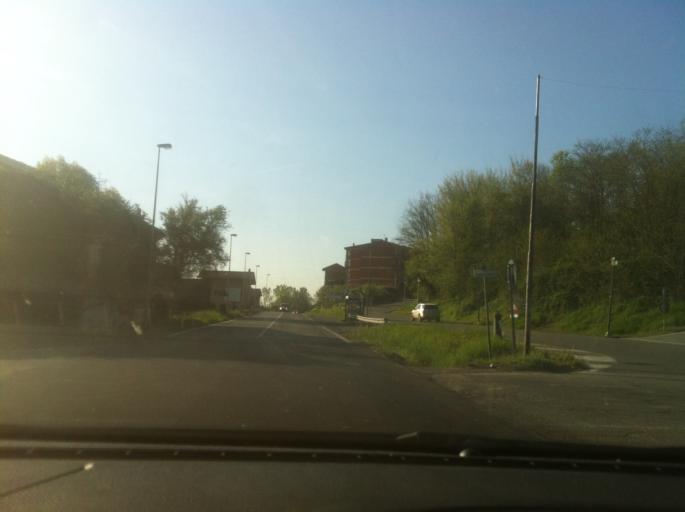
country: IT
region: Piedmont
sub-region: Provincia di Torino
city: Mercenasco
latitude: 45.3608
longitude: 7.8807
